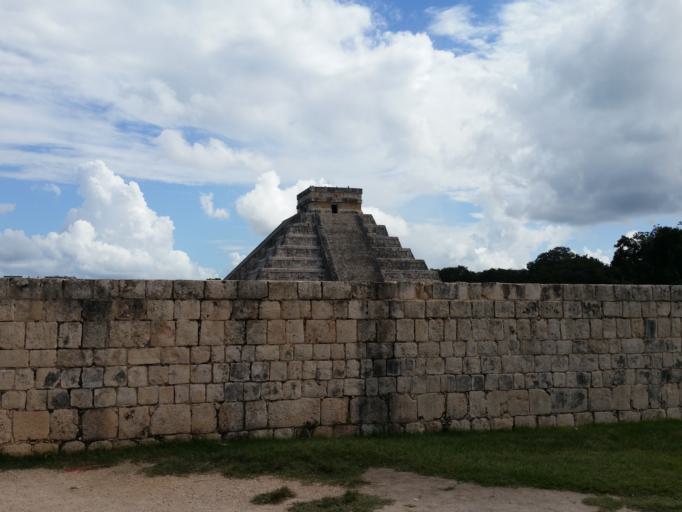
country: MX
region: Yucatan
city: Chichen-Itza
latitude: 20.6839
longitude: -88.5700
